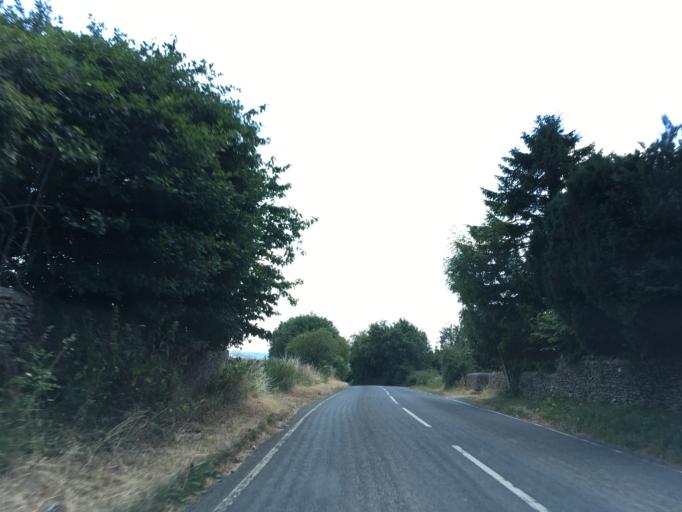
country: GB
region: England
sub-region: Gloucestershire
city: Stroud
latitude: 51.7712
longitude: -2.2355
